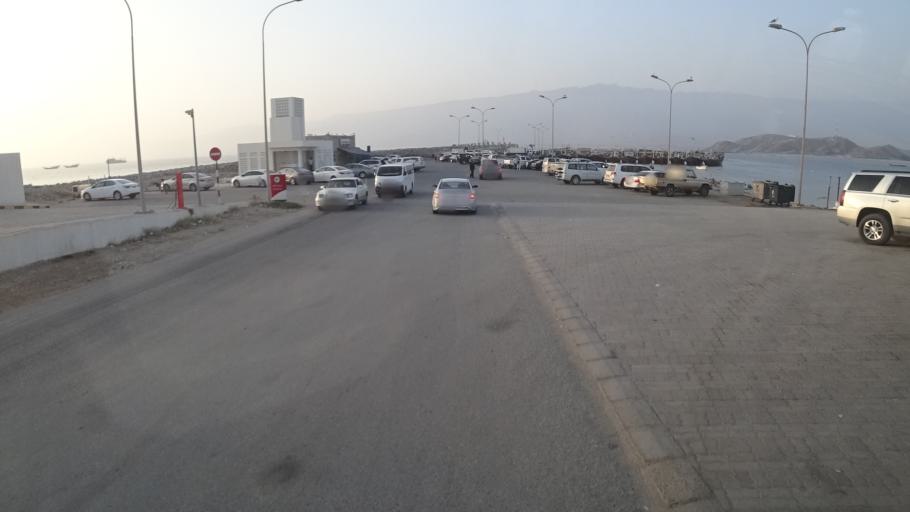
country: OM
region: Zufar
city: Salalah
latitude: 16.9854
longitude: 54.6868
